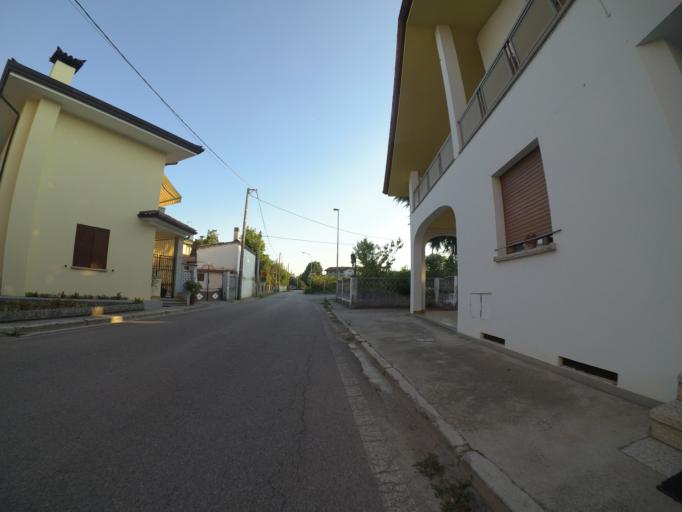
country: IT
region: Friuli Venezia Giulia
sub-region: Provincia di Udine
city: Campoformido
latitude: 46.0169
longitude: 13.1573
